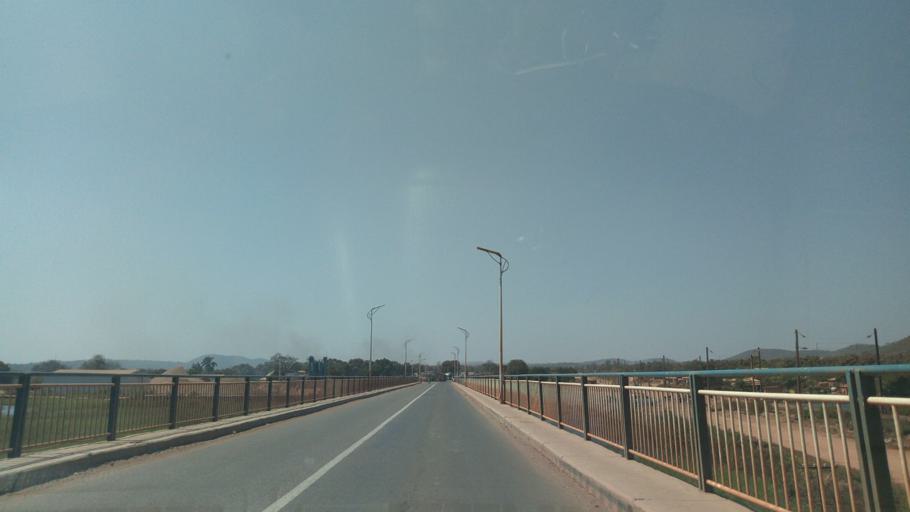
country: CD
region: Katanga
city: Kolwezi
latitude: -10.7807
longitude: 25.7281
